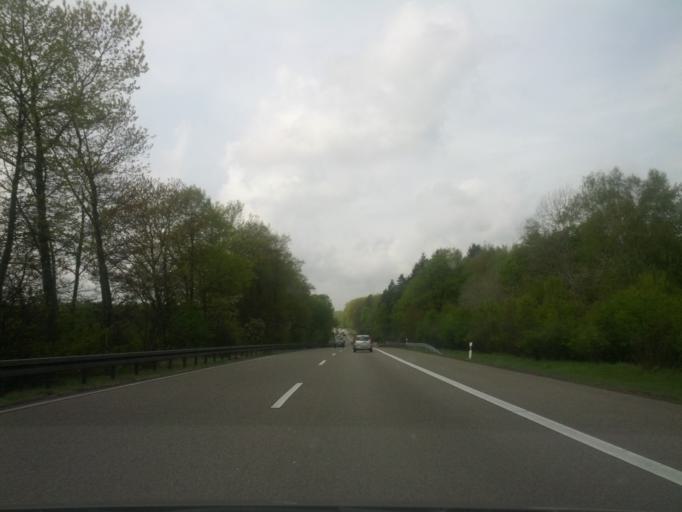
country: DE
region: Hesse
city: Kirtorf
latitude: 50.7148
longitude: 9.1035
